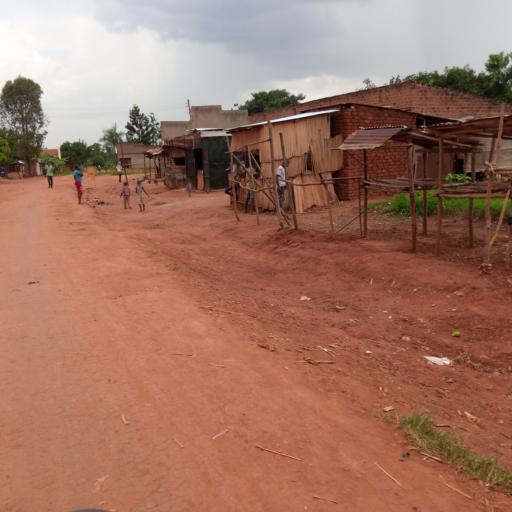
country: UG
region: Eastern Region
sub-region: Mbale District
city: Mbale
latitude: 1.1243
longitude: 34.1838
